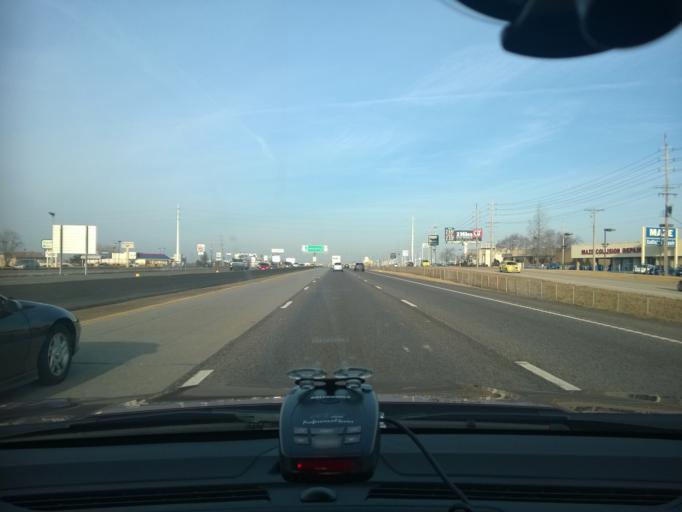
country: US
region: Missouri
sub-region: Saint Charles County
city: Saint Peters
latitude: 38.7960
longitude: -90.5729
